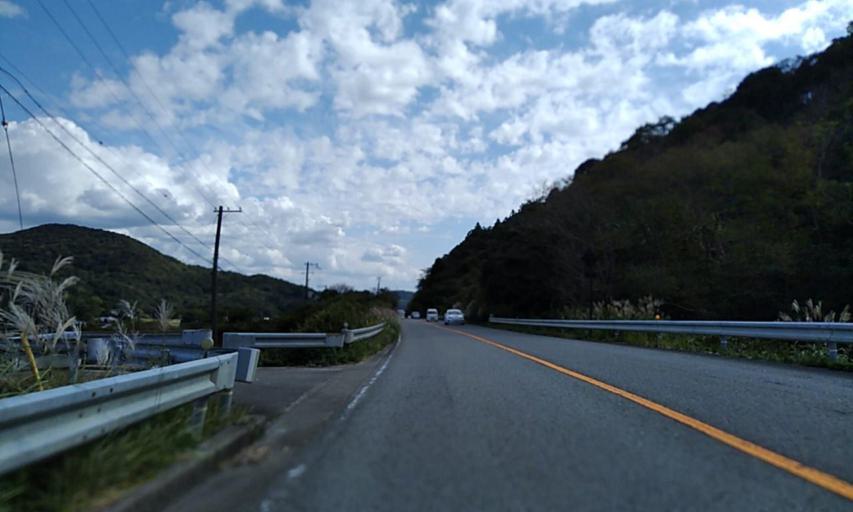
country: JP
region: Wakayama
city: Gobo
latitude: 33.9362
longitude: 135.1352
